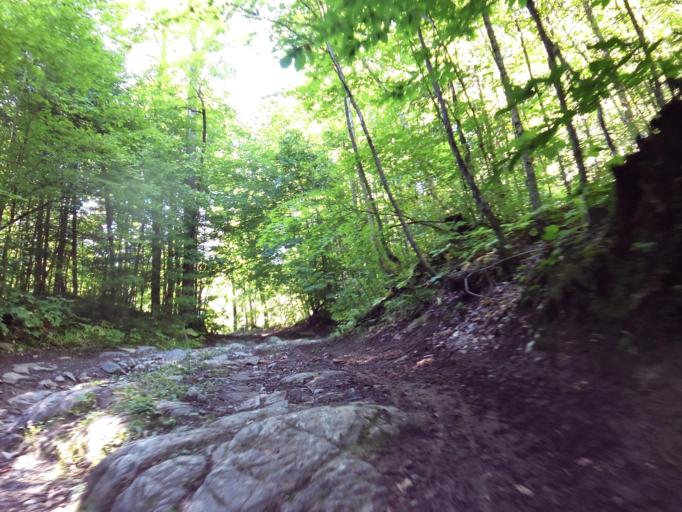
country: CA
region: Ontario
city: Renfrew
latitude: 45.1276
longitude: -76.7417
